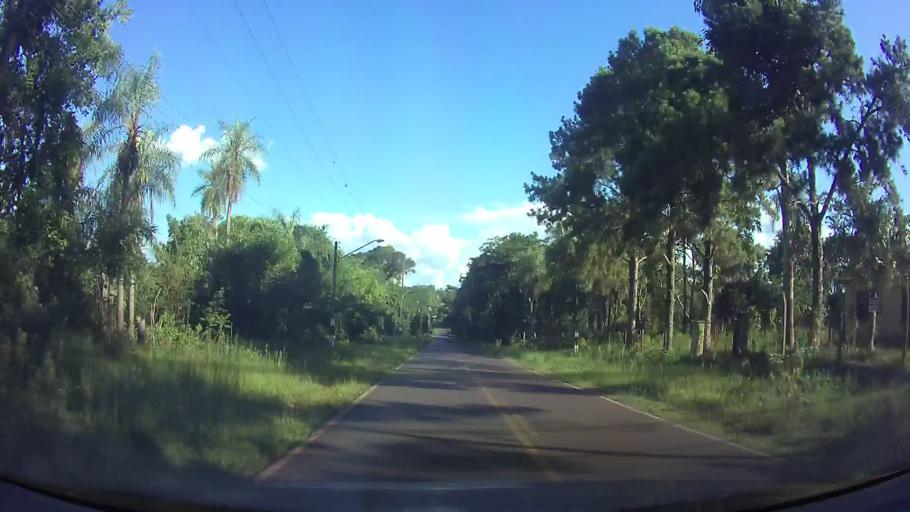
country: PY
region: Central
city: Aregua
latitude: -25.3242
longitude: -57.3898
